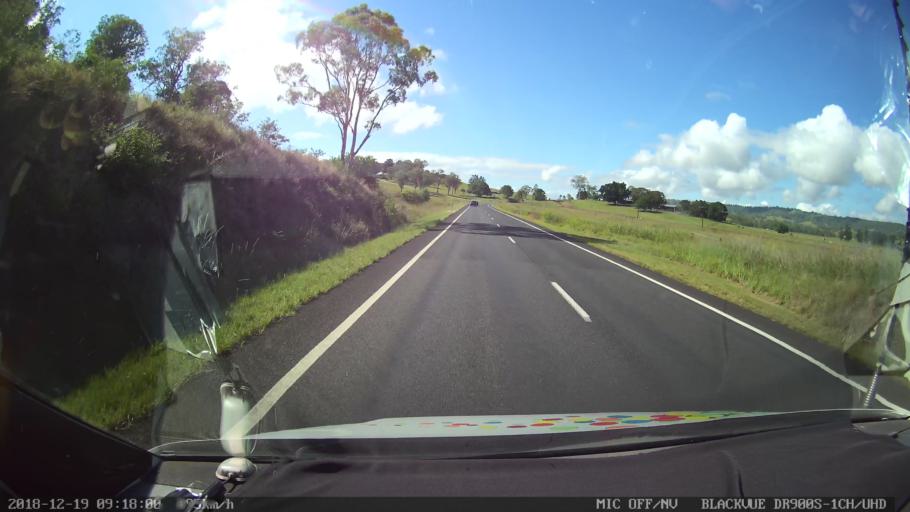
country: AU
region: New South Wales
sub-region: Kyogle
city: Kyogle
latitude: -28.5416
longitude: 152.9759
